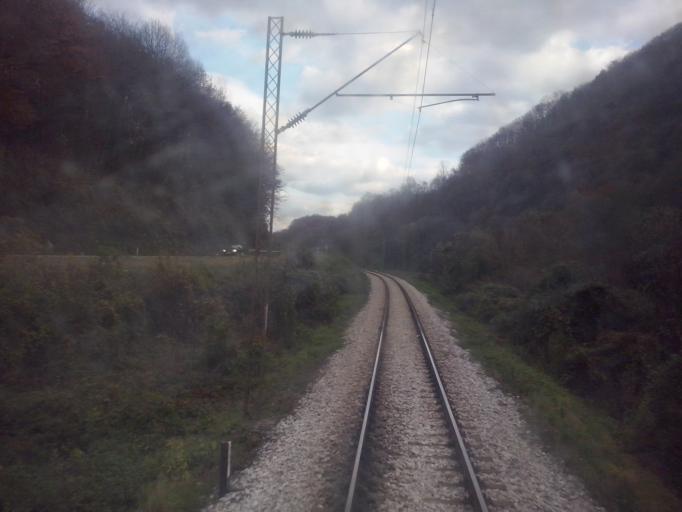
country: RS
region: Central Serbia
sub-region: Zlatiborski Okrug
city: Pozega
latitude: 43.8107
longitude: 19.9917
